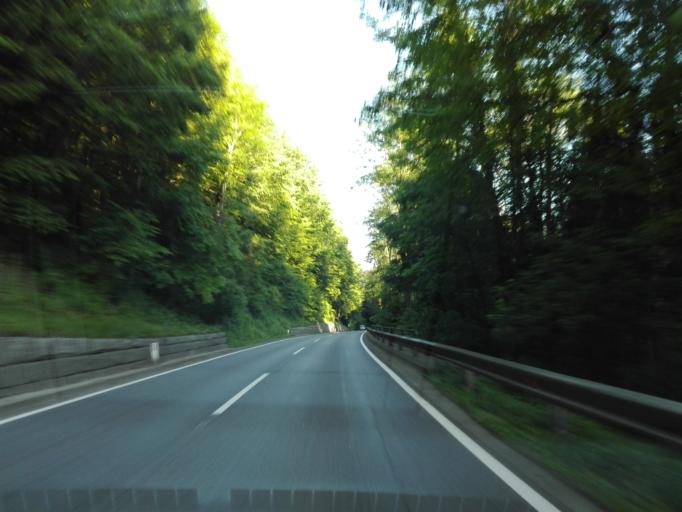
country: AT
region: Upper Austria
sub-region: Politischer Bezirk Rohrbach
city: Kleinzell im Muehlkreis
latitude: 48.3907
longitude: 13.9326
